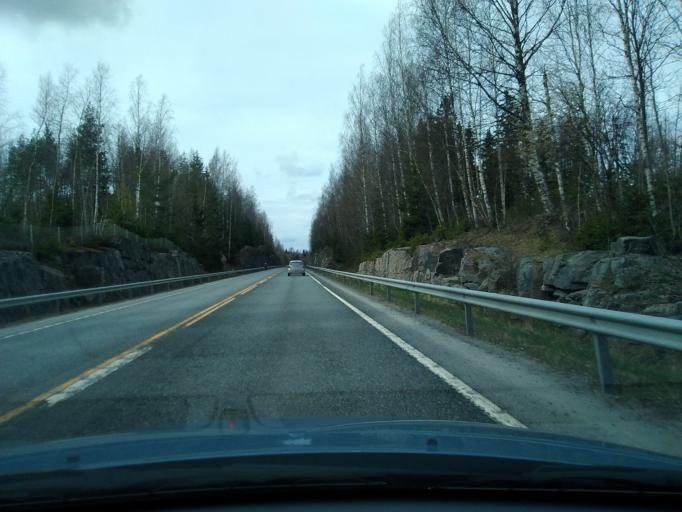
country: FI
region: Uusimaa
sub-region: Porvoo
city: Porvoo
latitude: 60.4047
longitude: 25.5900
